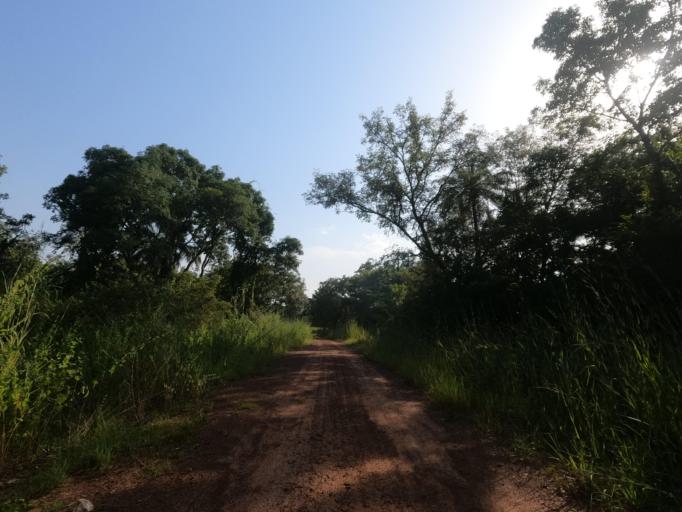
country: SN
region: Sedhiou
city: Sedhiou
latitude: 12.4378
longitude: -15.7381
